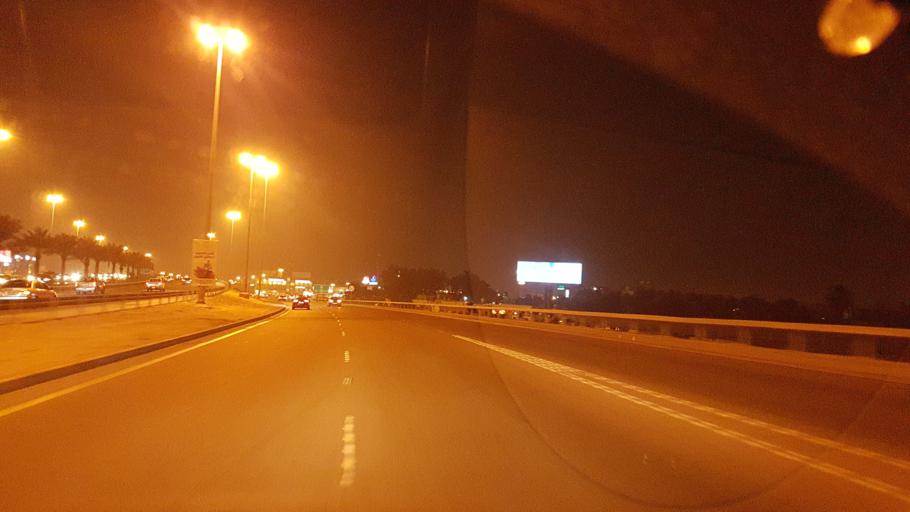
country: BH
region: Manama
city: Jidd Hafs
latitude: 26.2223
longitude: 50.5222
